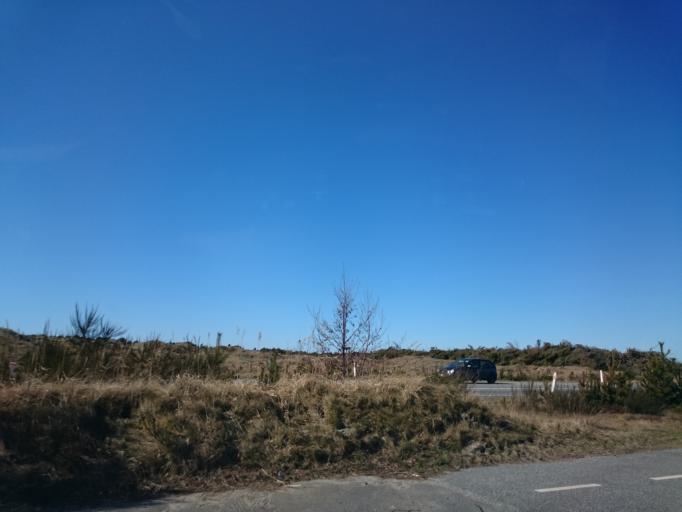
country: DK
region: North Denmark
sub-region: Frederikshavn Kommune
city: Skagen
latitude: 57.6664
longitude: 10.4550
